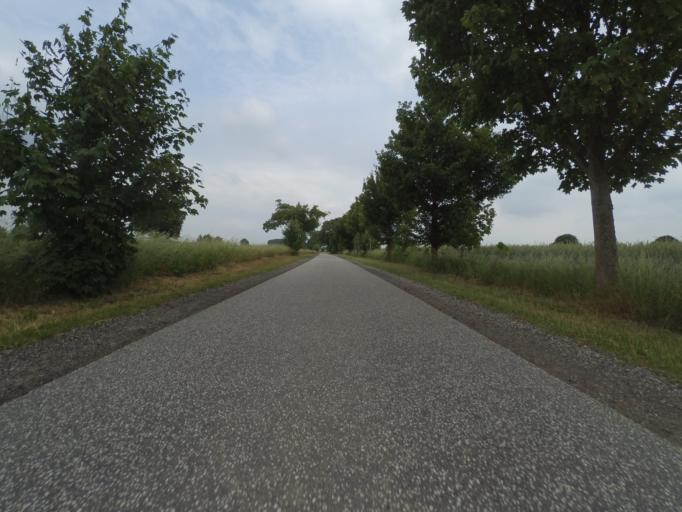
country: DE
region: Mecklenburg-Vorpommern
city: Plau am See
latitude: 53.4444
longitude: 12.2221
